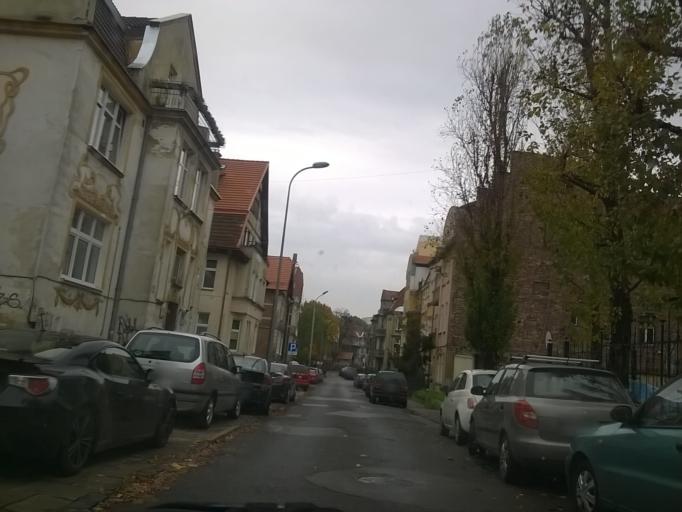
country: PL
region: Pomeranian Voivodeship
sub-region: Gdansk
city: Gdansk
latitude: 54.3743
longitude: 18.6171
